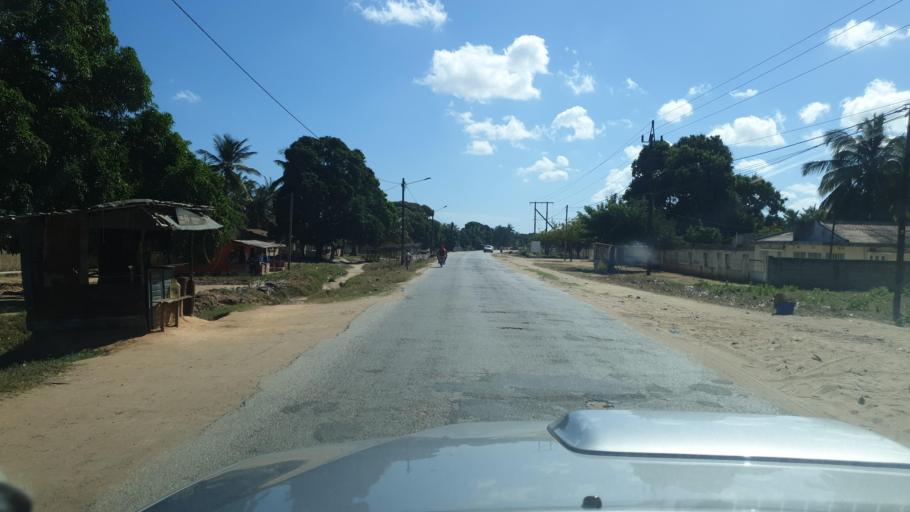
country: MZ
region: Nampula
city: Nacala
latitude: -14.5202
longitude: 40.6955
